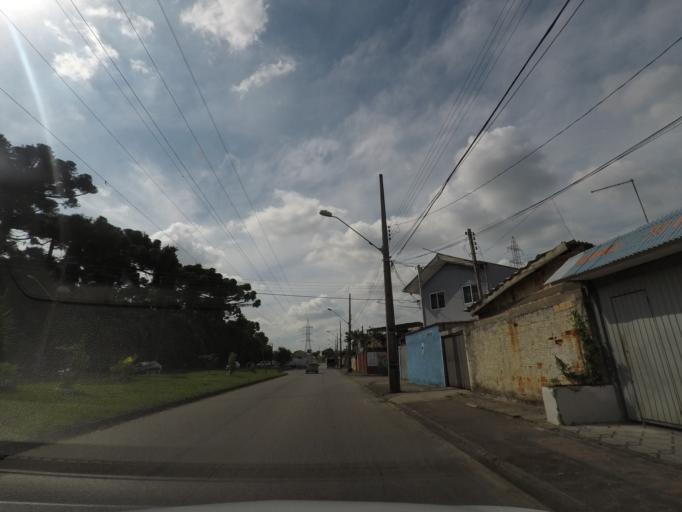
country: BR
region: Parana
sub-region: Sao Jose Dos Pinhais
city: Sao Jose dos Pinhais
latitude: -25.4915
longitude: -49.2072
